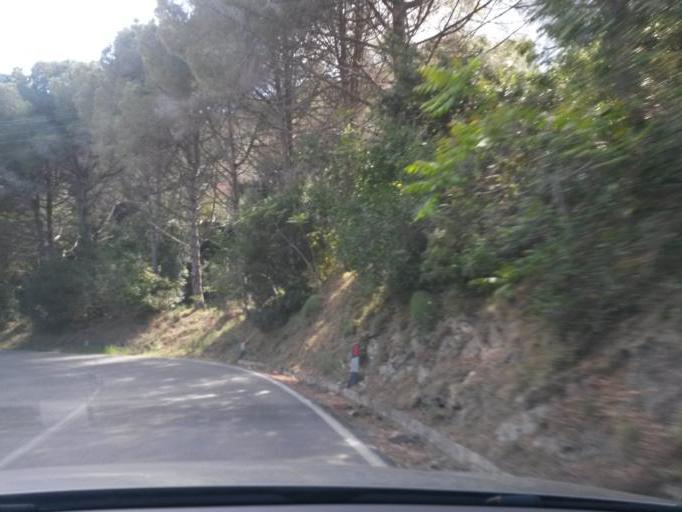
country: IT
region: Tuscany
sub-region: Provincia di Livorno
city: Marciana Marina
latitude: 42.7943
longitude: 10.2175
